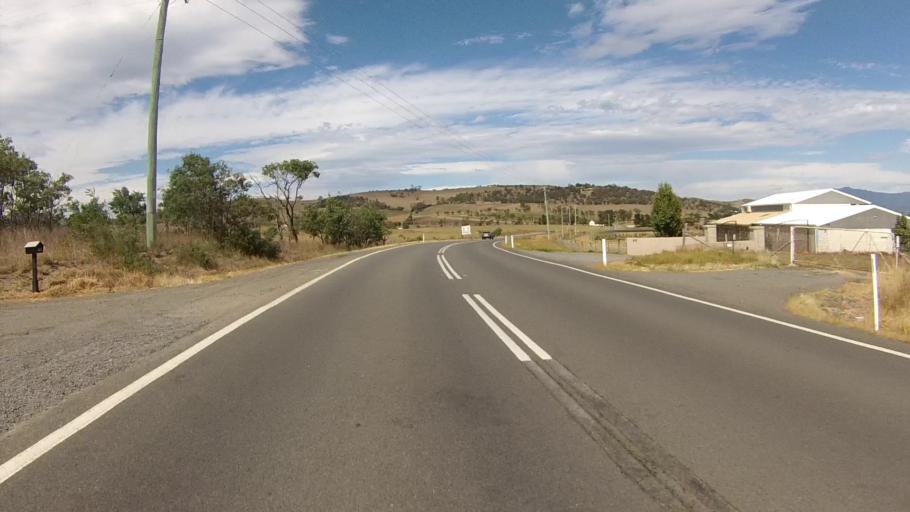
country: AU
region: Tasmania
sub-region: Brighton
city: Old Beach
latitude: -42.6878
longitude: 147.3515
